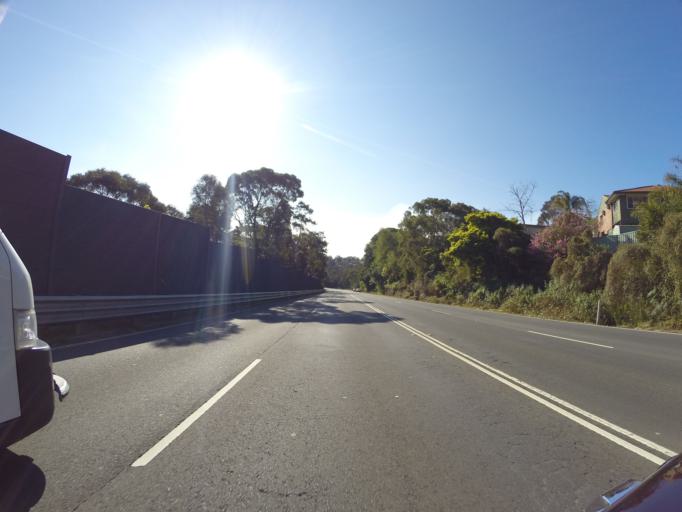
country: AU
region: New South Wales
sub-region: Sutherland Shire
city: Heathcote
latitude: -34.0767
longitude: 151.0074
